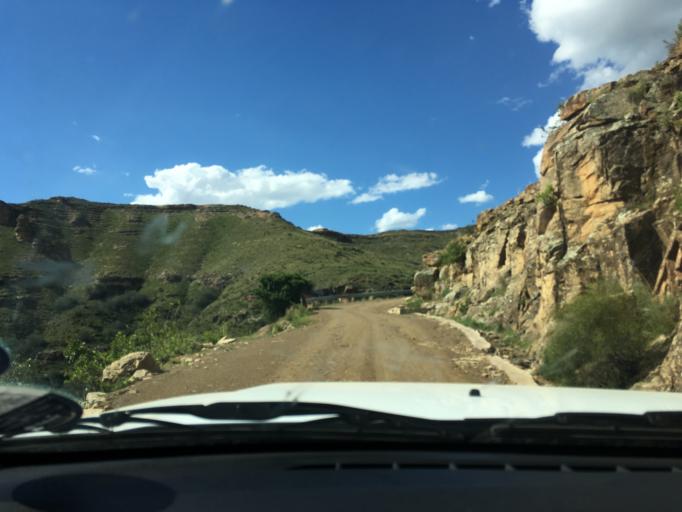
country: LS
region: Quthing
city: Quthing
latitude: -30.2323
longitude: 27.9662
